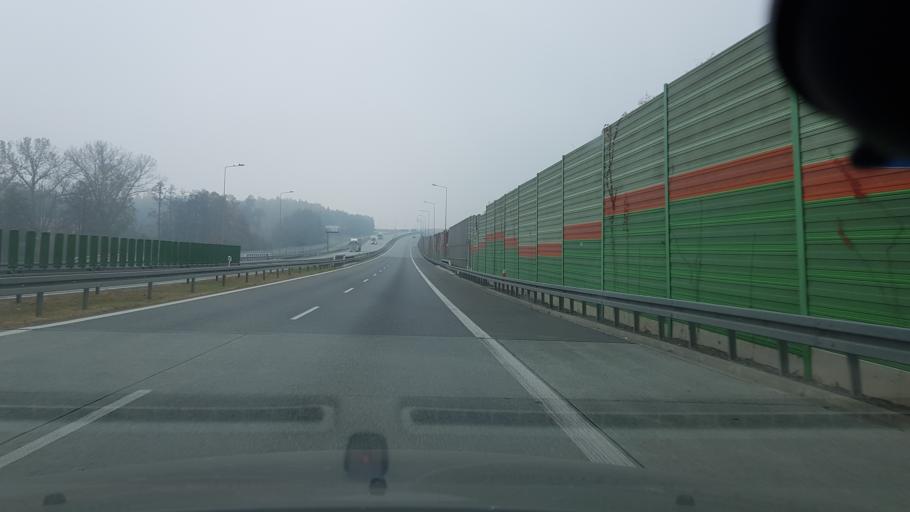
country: PL
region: Lodz Voivodeship
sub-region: Powiat rawski
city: Rawa Mazowiecka
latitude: 51.7103
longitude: 20.2188
